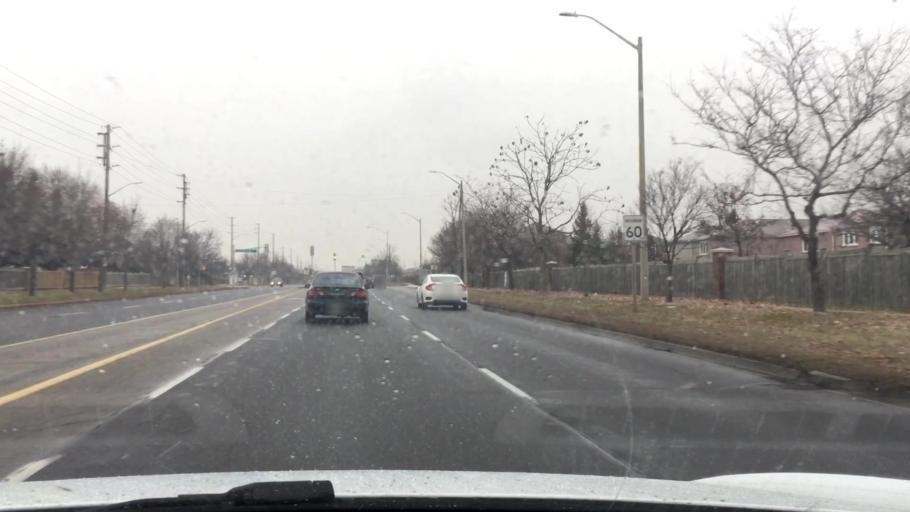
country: CA
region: Ontario
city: Markham
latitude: 43.8371
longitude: -79.2767
